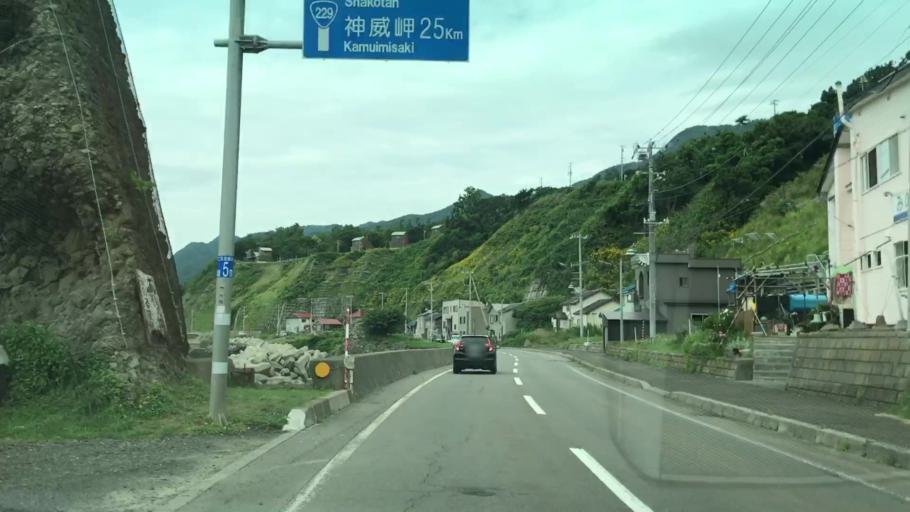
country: JP
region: Hokkaido
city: Iwanai
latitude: 43.1451
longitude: 140.4227
